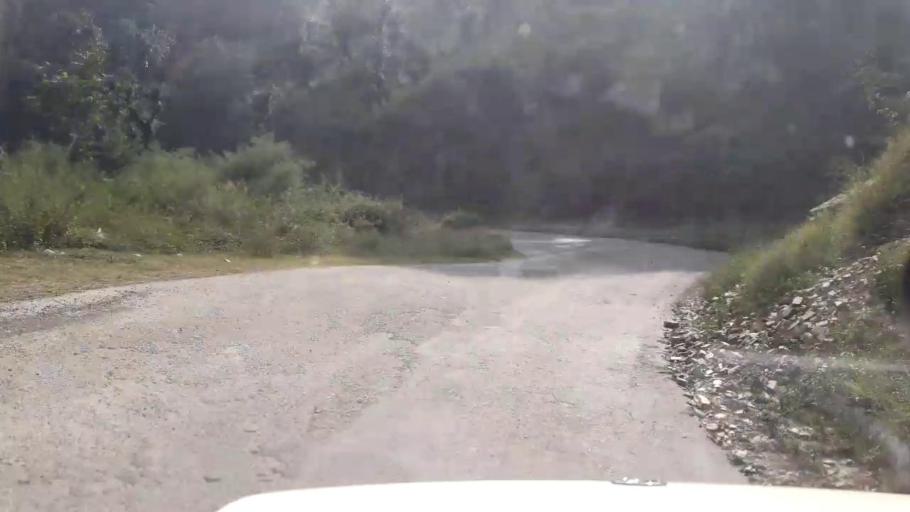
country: IN
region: Himachal Pradesh
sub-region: Shimla
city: Shimla
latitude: 31.0538
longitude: 77.1551
